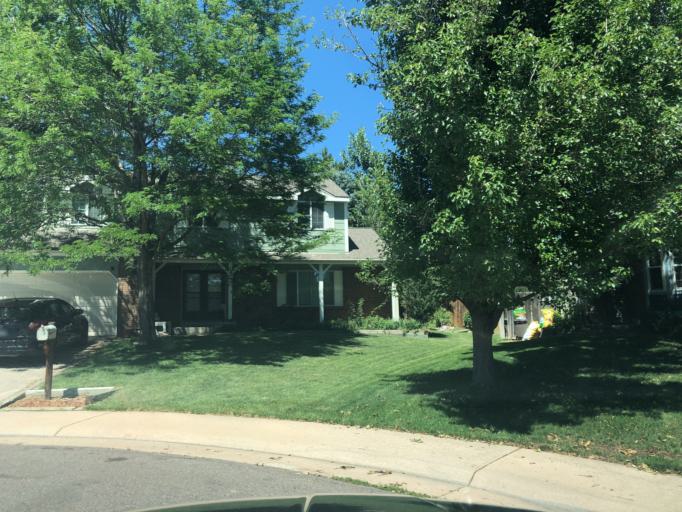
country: US
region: Colorado
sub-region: Arapahoe County
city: Dove Valley
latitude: 39.6159
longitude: -104.7909
